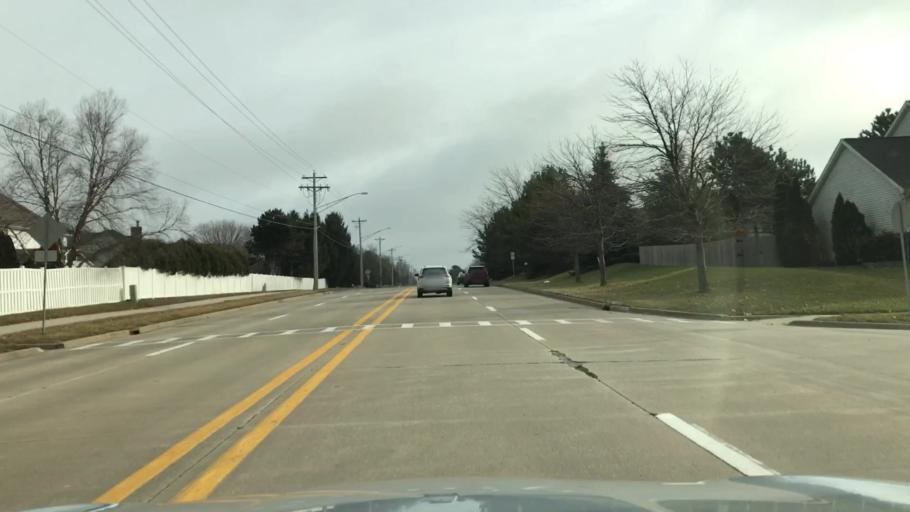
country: US
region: Illinois
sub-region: McLean County
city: Normal
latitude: 40.5026
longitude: -88.9140
